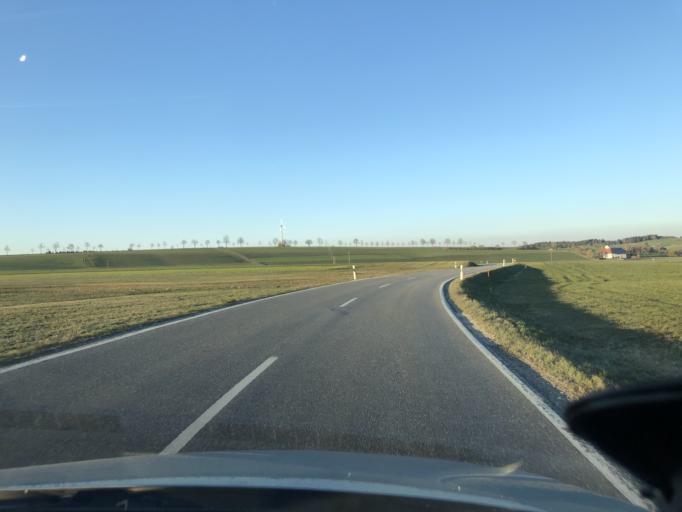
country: DE
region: Baden-Wuerttemberg
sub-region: Freiburg Region
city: Hufingen
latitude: 47.8850
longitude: 8.4751
